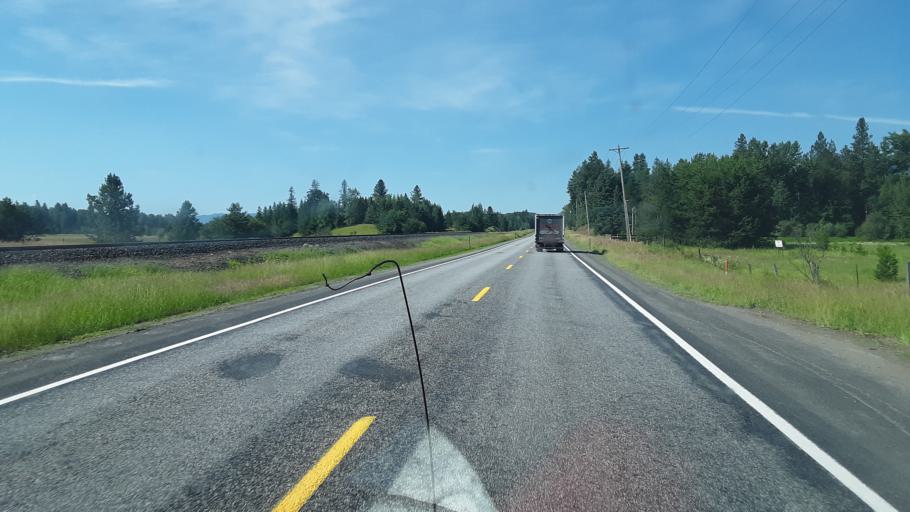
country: US
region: Idaho
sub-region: Bonner County
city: Ponderay
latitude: 48.4532
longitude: -116.4773
